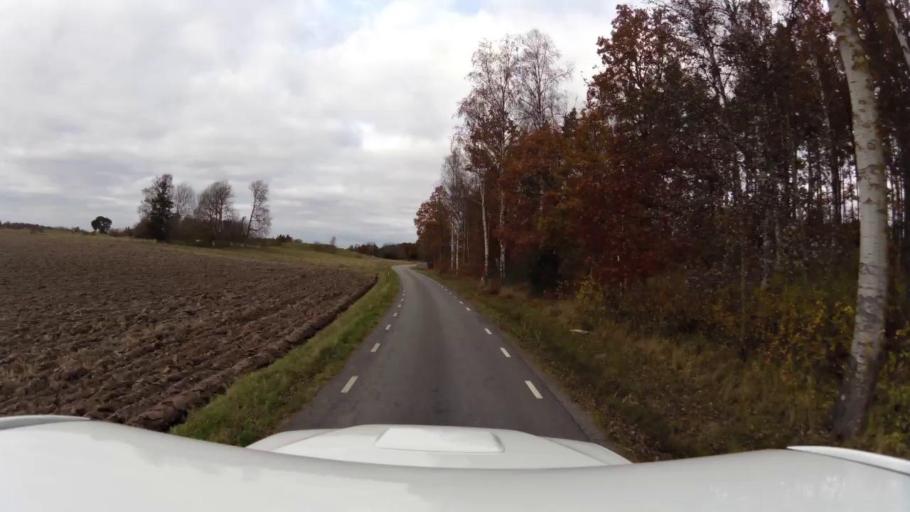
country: SE
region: OEstergoetland
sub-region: Linkopings Kommun
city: Linghem
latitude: 58.3886
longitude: 15.8122
